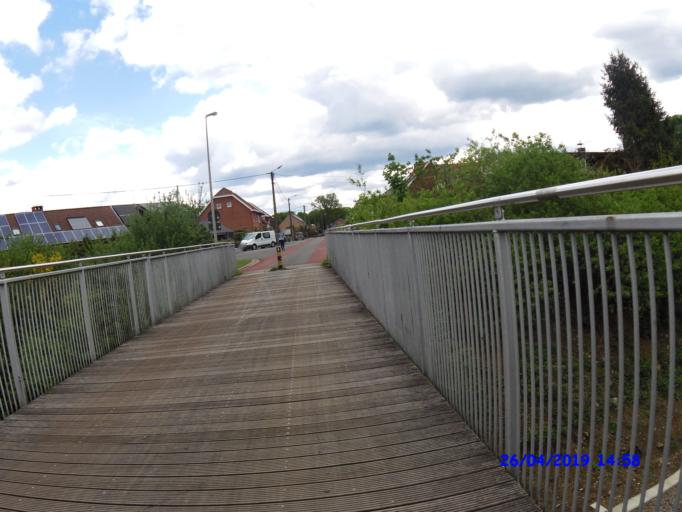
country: BE
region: Flanders
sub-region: Provincie Limburg
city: Beringen
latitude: 51.0516
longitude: 5.2338
